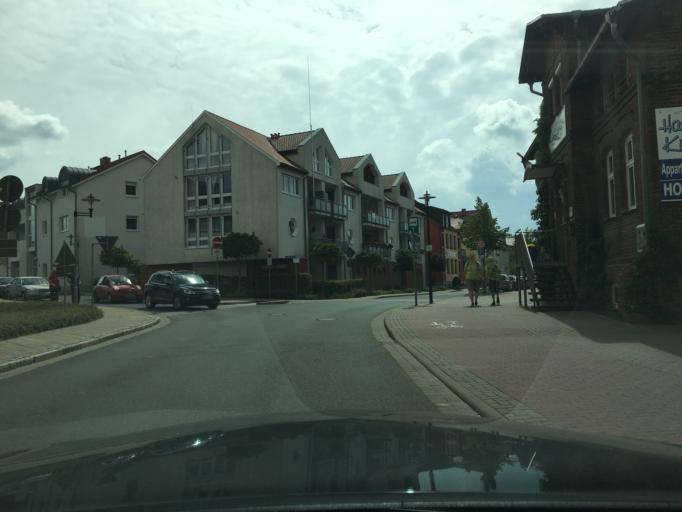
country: DE
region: Mecklenburg-Vorpommern
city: Waren
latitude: 53.5109
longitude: 12.6915
